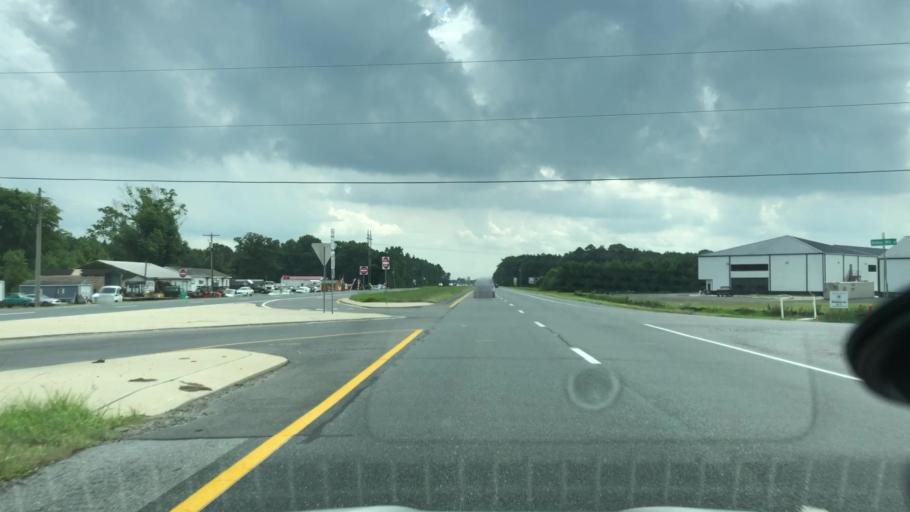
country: US
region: Delaware
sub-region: Sussex County
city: Delmar
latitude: 38.4787
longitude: -75.5579
